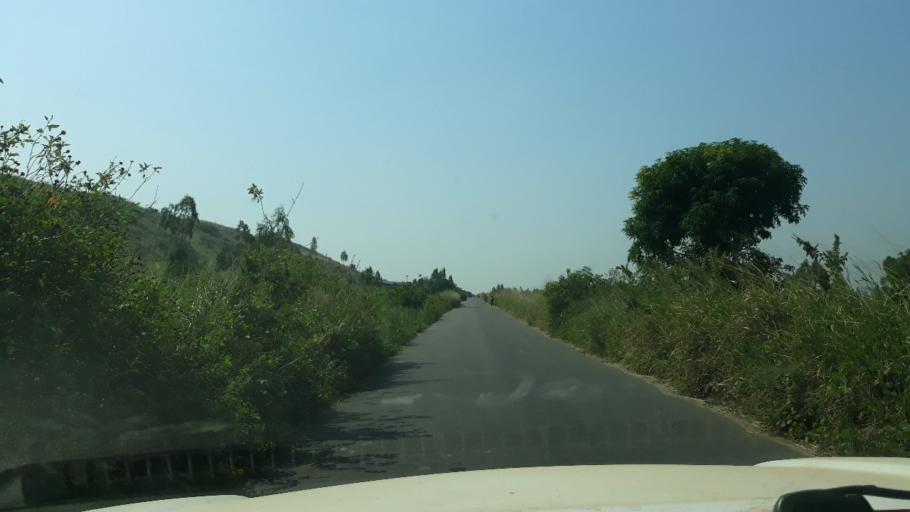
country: CD
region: South Kivu
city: Uvira
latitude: -3.2720
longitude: 29.1613
